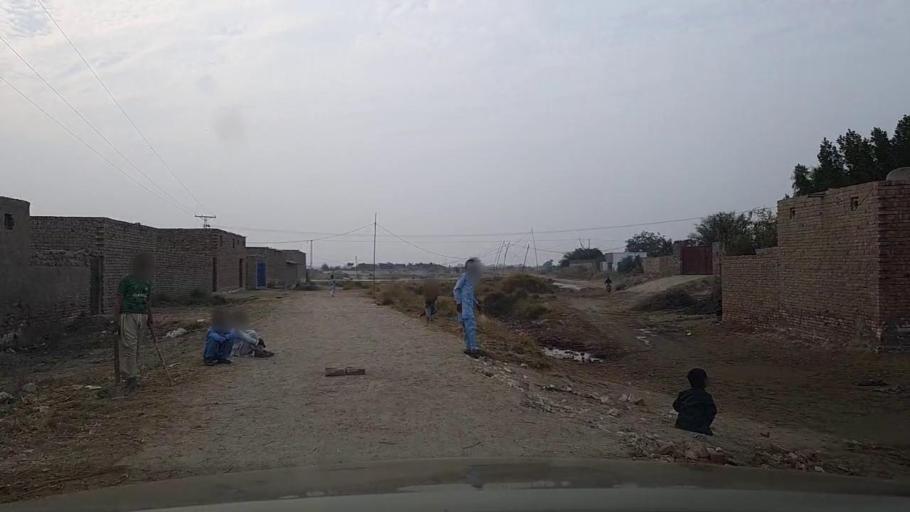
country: PK
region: Sindh
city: Sanghar
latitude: 26.1973
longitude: 68.9636
